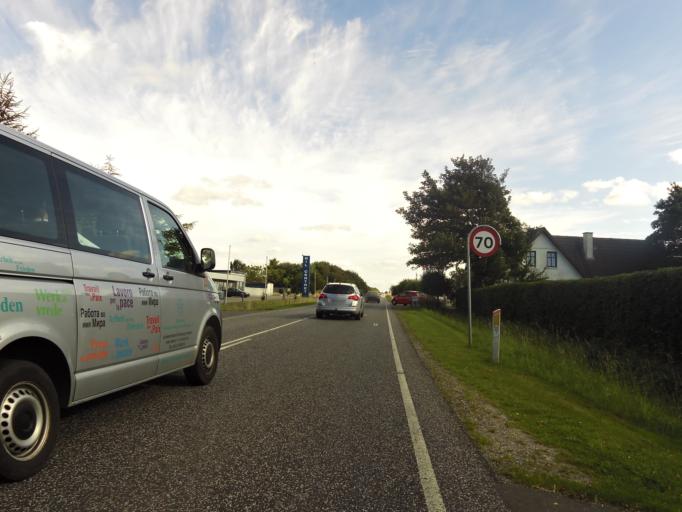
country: DK
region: South Denmark
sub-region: Tonder Kommune
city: Toftlund
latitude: 55.1918
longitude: 9.0544
